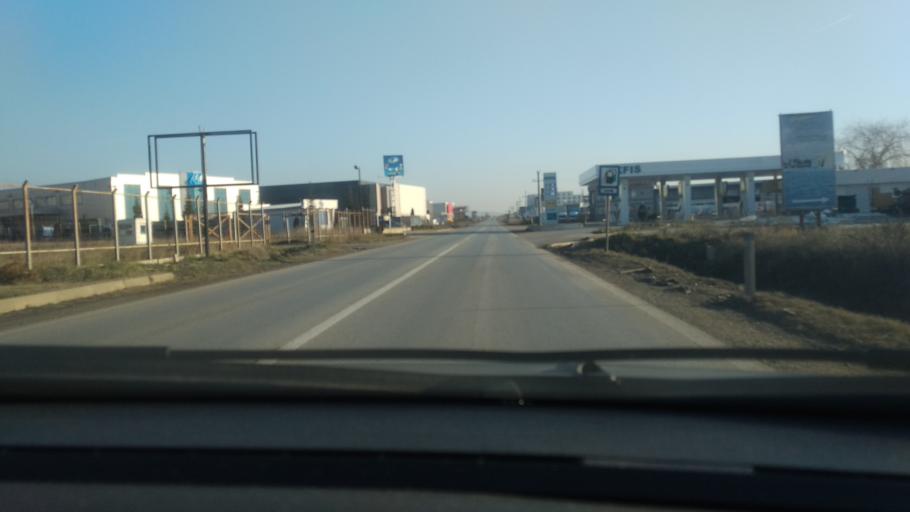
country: XK
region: Pristina
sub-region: Lipjan
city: Lipljan
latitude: 42.5588
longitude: 21.1368
